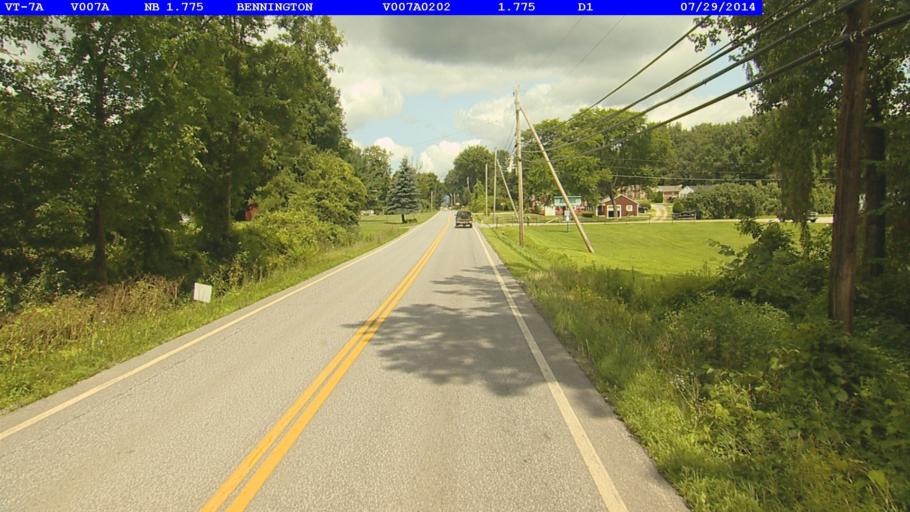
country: US
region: Vermont
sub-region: Bennington County
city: North Bennington
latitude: 42.9153
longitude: -73.2110
